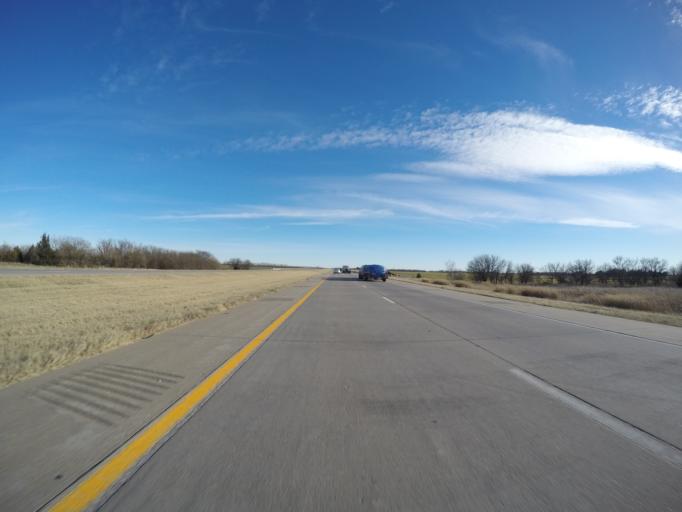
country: US
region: Kansas
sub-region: McPherson County
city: Moundridge
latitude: 38.2688
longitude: -97.5644
